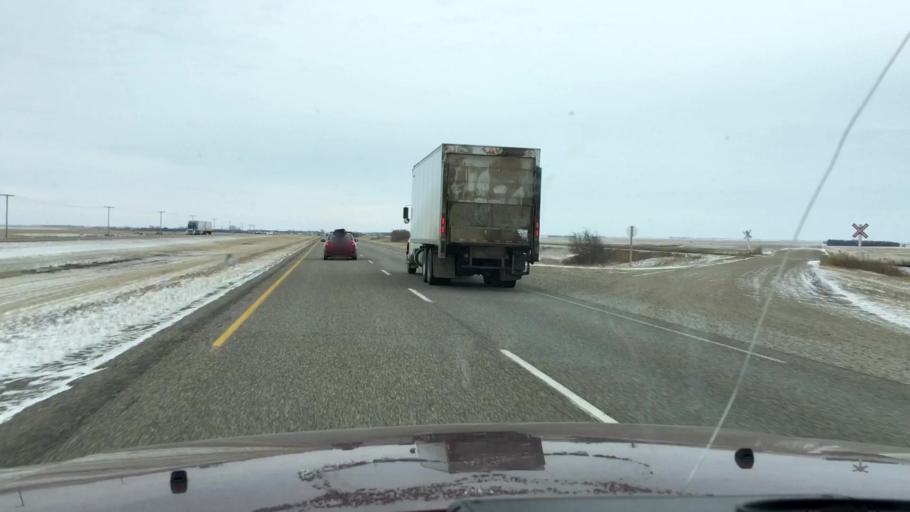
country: CA
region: Saskatchewan
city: Watrous
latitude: 51.1793
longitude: -105.9383
